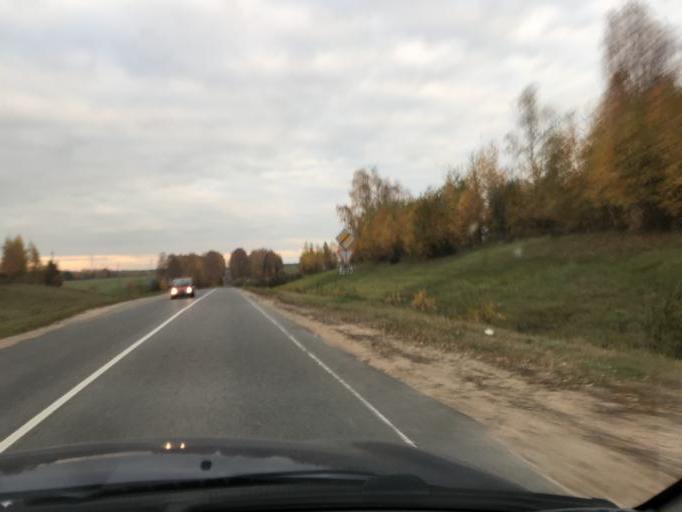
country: BY
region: Minsk
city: Hatava
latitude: 53.7678
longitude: 27.6331
